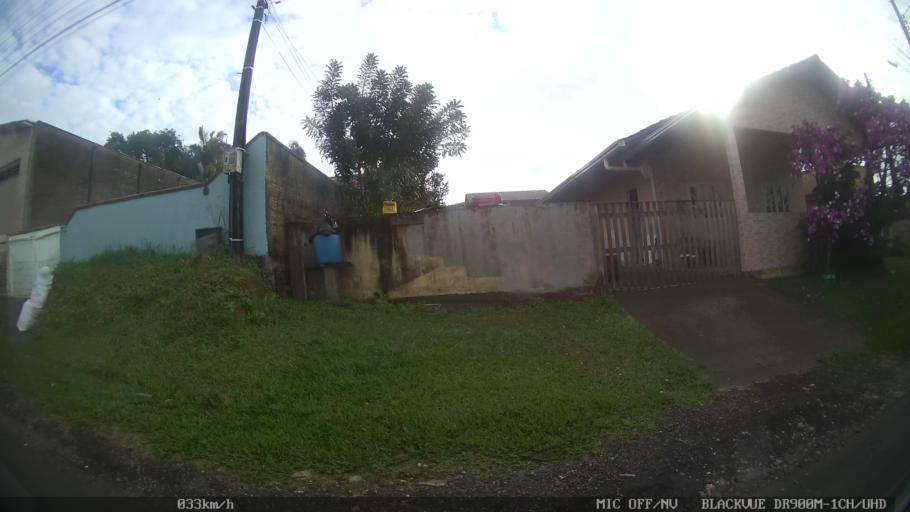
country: BR
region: Santa Catarina
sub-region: Barra Velha
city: Barra Velha
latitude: -26.6202
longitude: -48.7139
